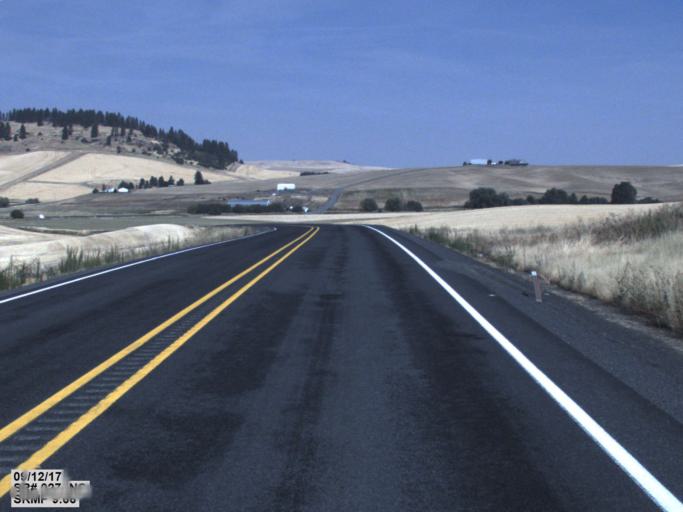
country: US
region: Washington
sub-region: Whitman County
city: Pullman
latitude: 46.8512
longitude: -117.1251
